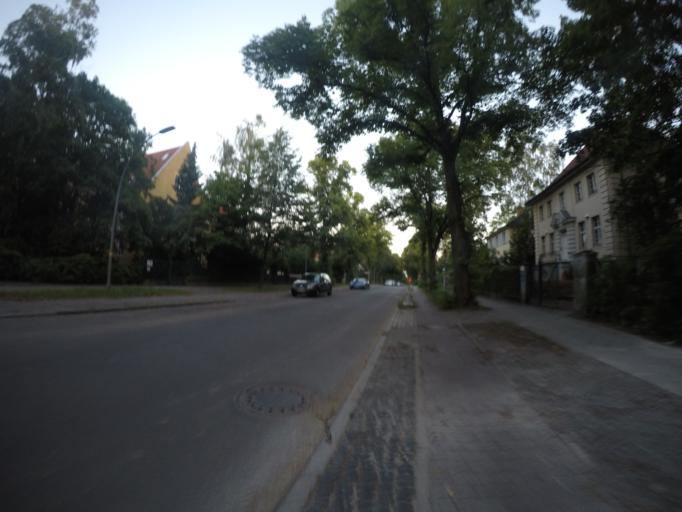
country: DE
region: Berlin
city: Dahlem
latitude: 52.4531
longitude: 13.2936
